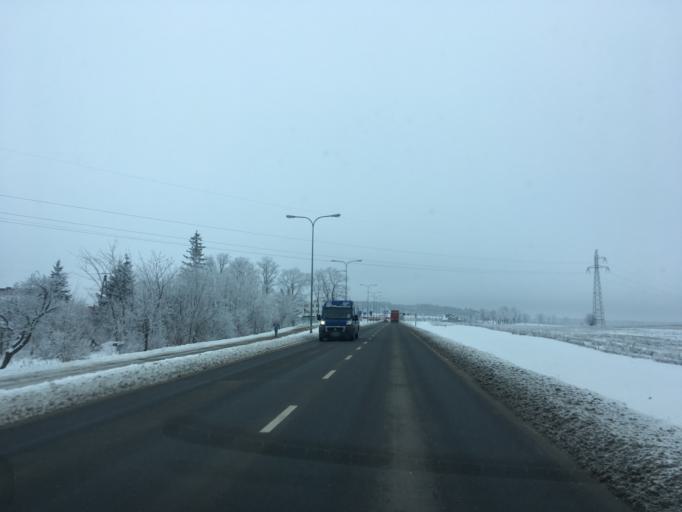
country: PL
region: Warmian-Masurian Voivodeship
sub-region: Powiat dzialdowski
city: Dzialdowo
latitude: 53.2502
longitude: 20.1911
